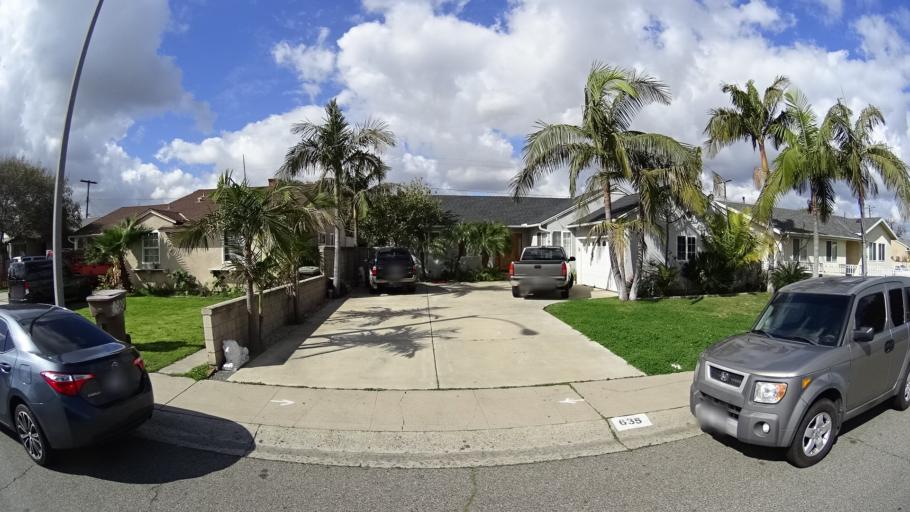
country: US
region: California
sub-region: Orange County
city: Anaheim
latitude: 33.8457
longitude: -117.9001
